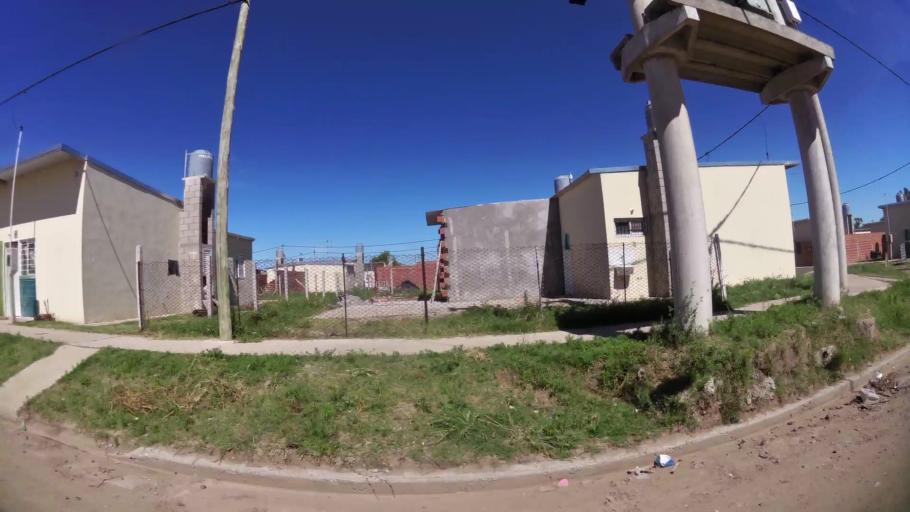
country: AR
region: Santa Fe
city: Perez
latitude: -32.9761
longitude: -60.7048
